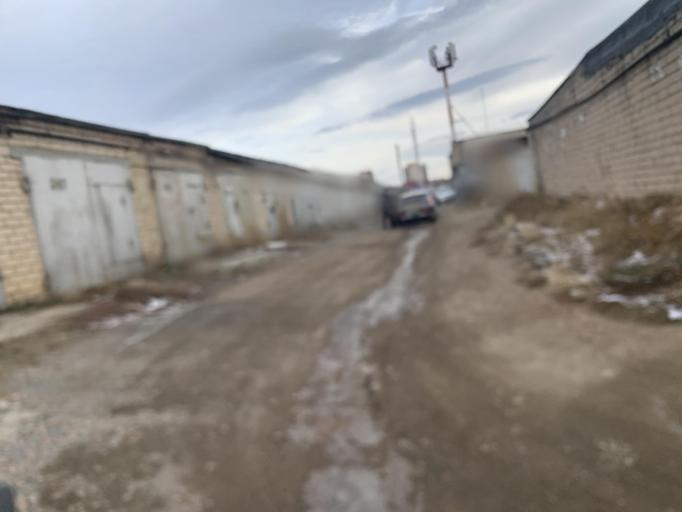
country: RU
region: Chelyabinsk
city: Roshchino
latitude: 55.1853
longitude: 61.2653
